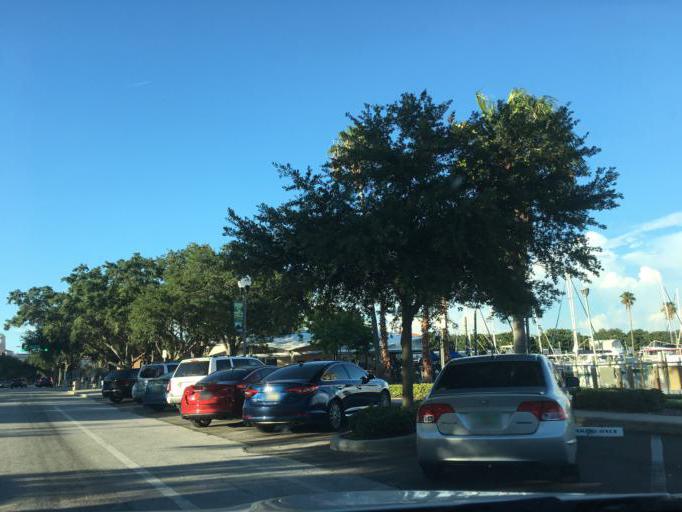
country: US
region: Florida
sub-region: Pinellas County
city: Saint Petersburg
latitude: 27.7728
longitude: -82.6318
